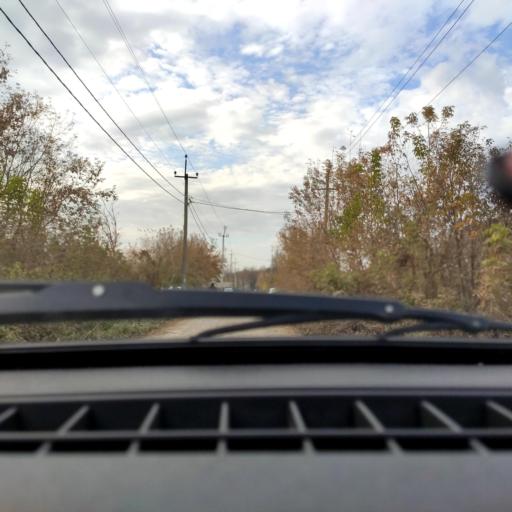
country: RU
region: Bashkortostan
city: Ufa
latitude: 54.7714
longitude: 55.9341
